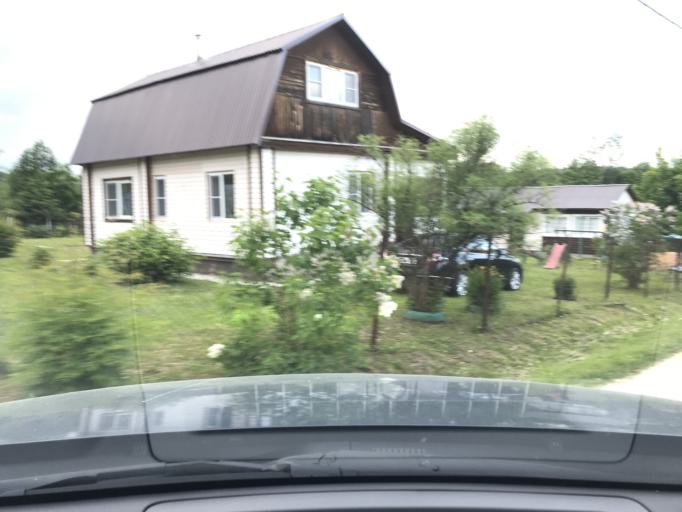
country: RU
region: Moskovskaya
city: Vereya
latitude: 55.3215
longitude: 36.3366
